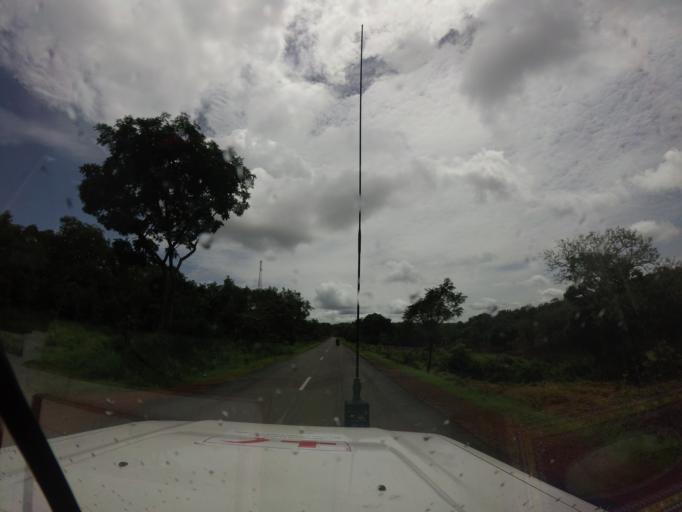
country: GN
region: Faranah
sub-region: Faranah Prefecture
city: Faranah
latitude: 10.0333
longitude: -10.9810
